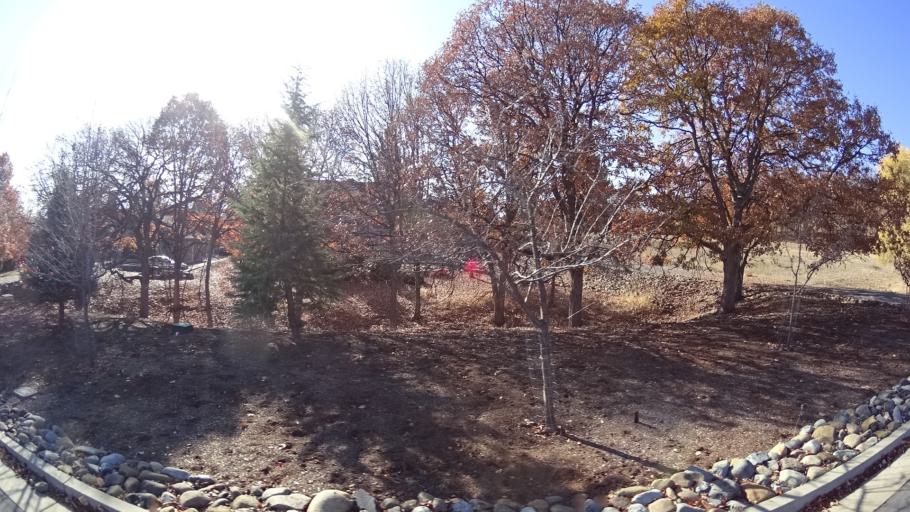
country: US
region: California
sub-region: Siskiyou County
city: Yreka
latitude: 41.7245
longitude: -122.6516
